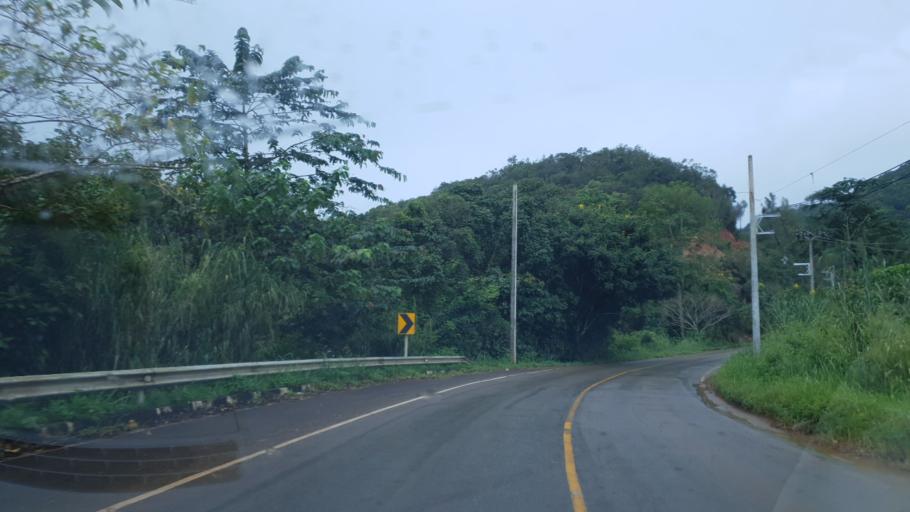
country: TH
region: Mae Hong Son
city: Ban Huai I Huak
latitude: 18.1478
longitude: 98.0735
